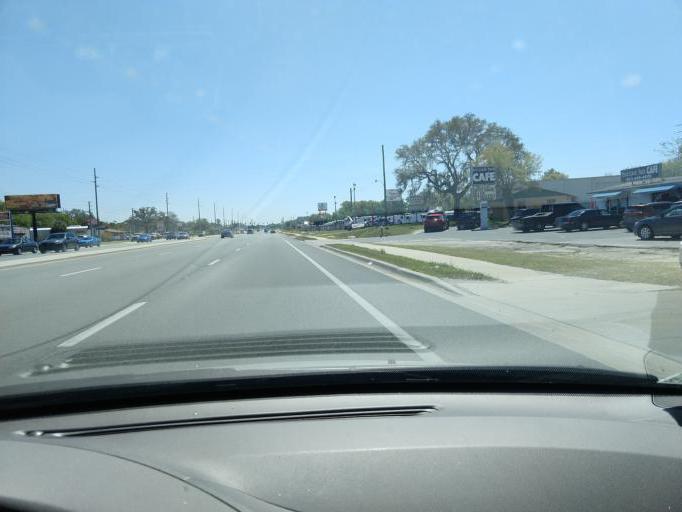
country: US
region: Florida
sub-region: Lake County
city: Fruitland Park
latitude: 28.8540
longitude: -81.9028
